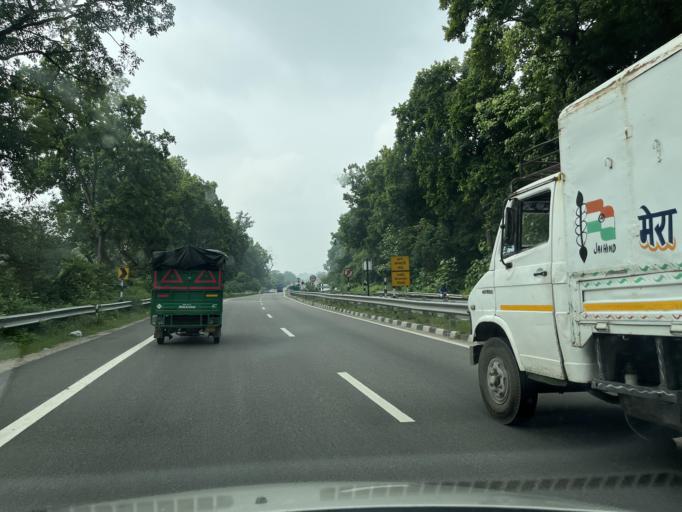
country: IN
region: Uttarakhand
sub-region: Dehradun
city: Raiwala
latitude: 30.0179
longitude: 78.1999
